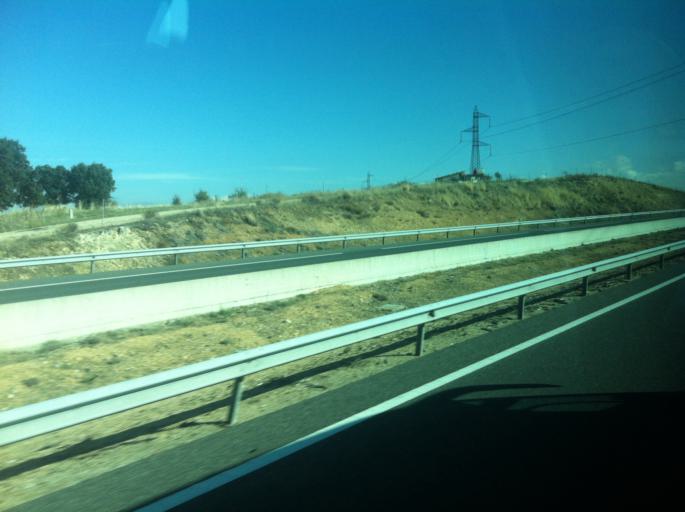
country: ES
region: Castille and Leon
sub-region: Provincia de Burgos
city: Aranda de Duero
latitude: 41.6479
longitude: -3.7177
